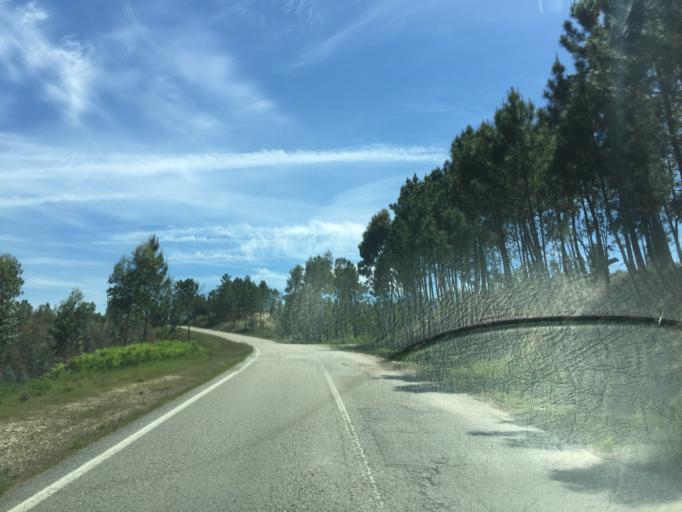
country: PT
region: Coimbra
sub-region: Soure
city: Soure
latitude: 40.0613
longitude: -8.6947
